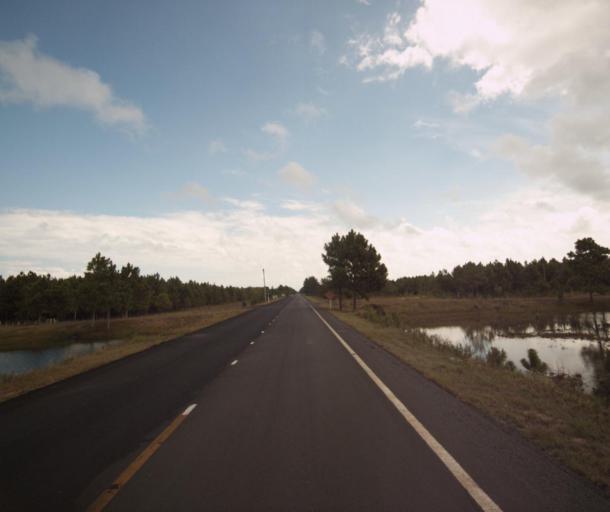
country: BR
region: Rio Grande do Sul
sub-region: Tapes
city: Tapes
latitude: -31.4242
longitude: -51.1824
